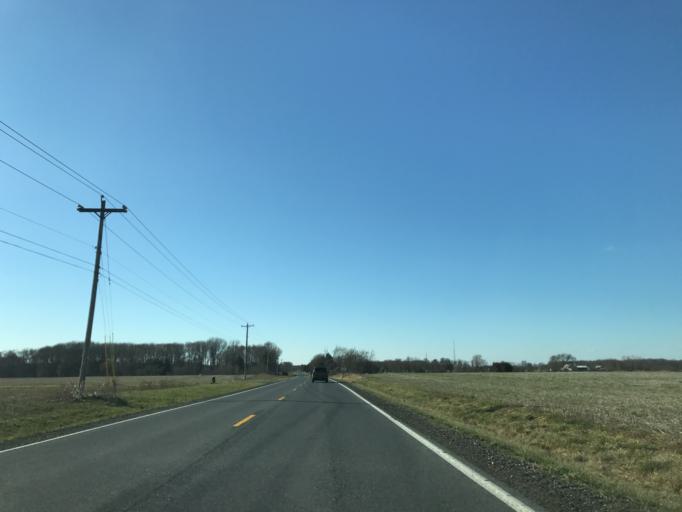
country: US
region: Maryland
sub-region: Queen Anne's County
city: Centreville
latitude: 39.0175
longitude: -76.0042
